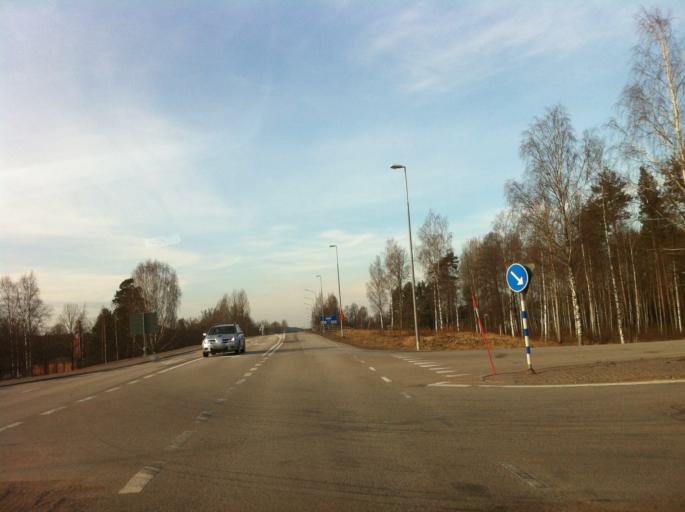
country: SE
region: Vaermland
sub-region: Storfors Kommun
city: Storfors
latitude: 59.5358
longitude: 14.2819
